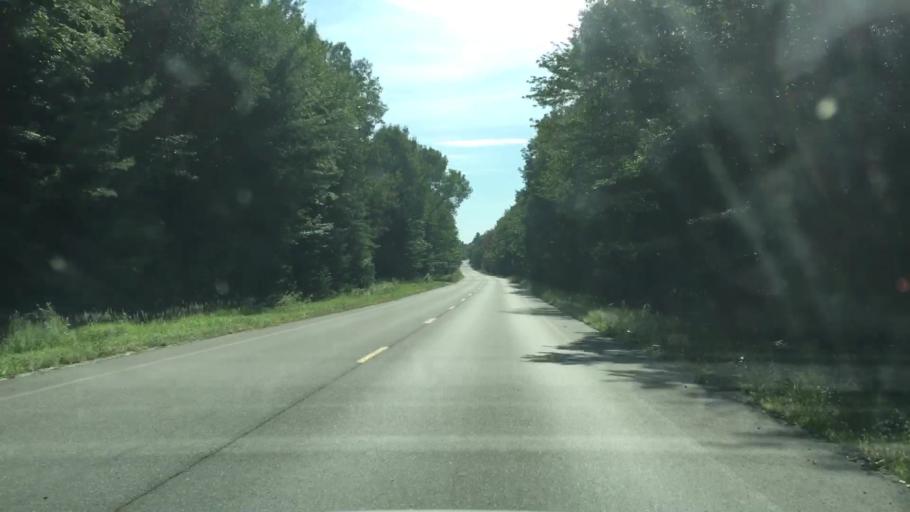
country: US
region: Maine
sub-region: Penobscot County
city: Lincoln
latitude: 45.3888
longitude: -68.5353
